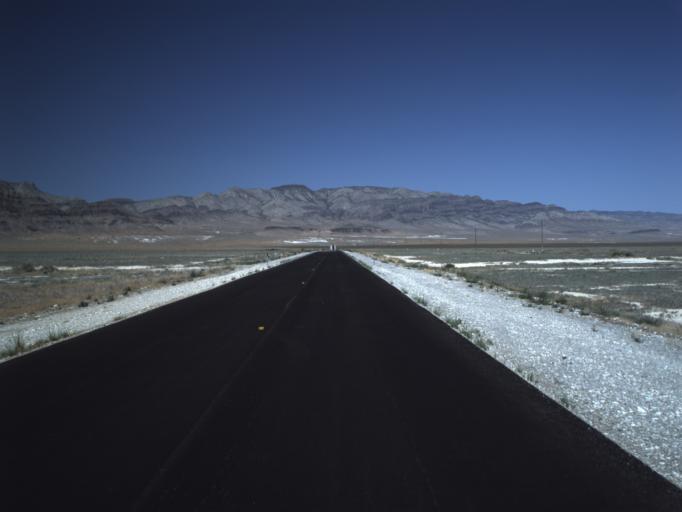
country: US
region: Utah
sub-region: Beaver County
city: Milford
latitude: 39.0651
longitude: -113.4476
